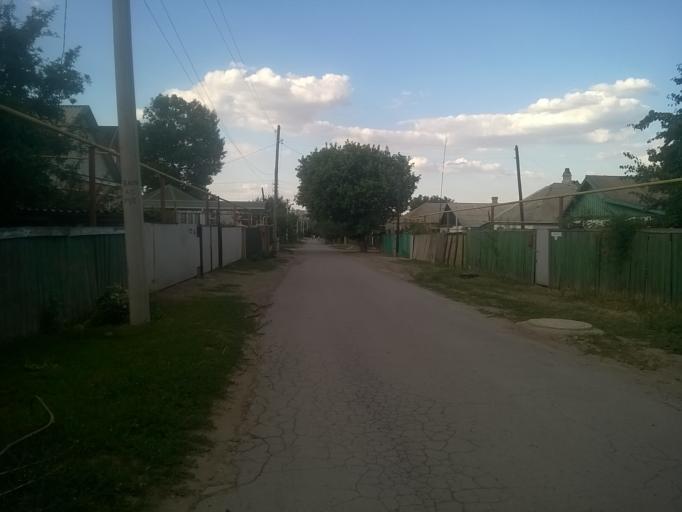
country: RU
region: Rostov
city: Donetsk
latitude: 48.3389
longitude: 39.9575
